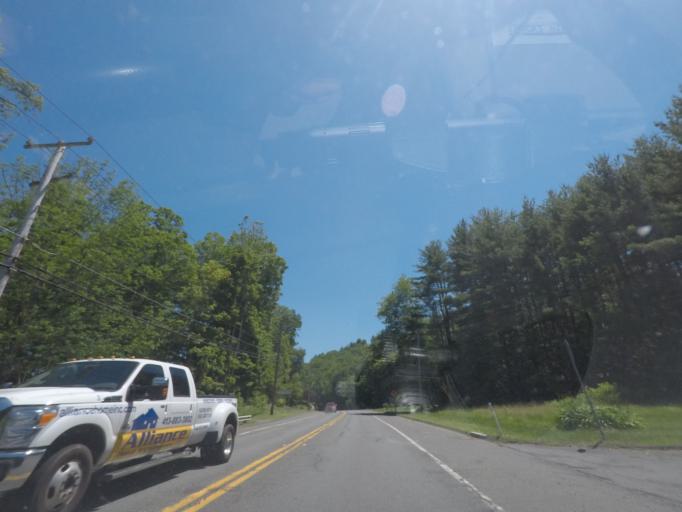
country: US
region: Massachusetts
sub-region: Hampden County
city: Granville
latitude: 42.1870
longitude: -72.8571
